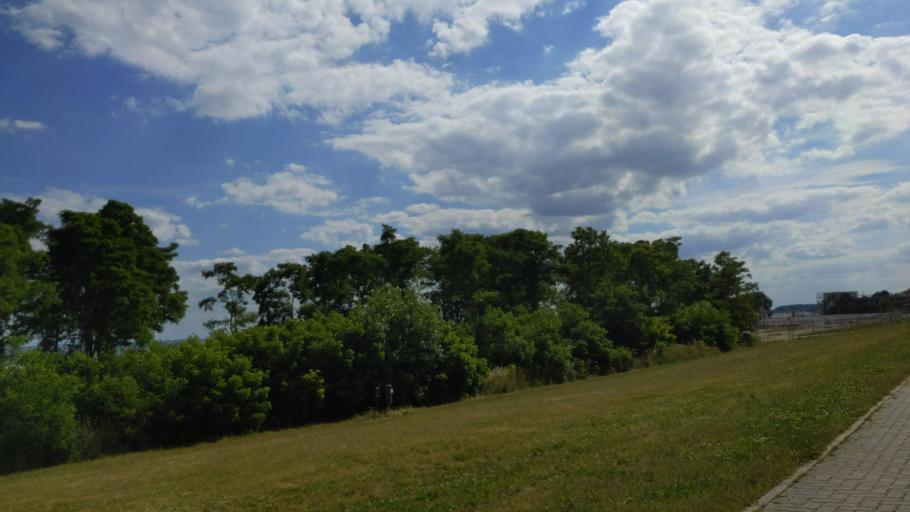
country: DE
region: Schleswig-Holstein
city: Gromitz
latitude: 54.1497
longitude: 10.9750
